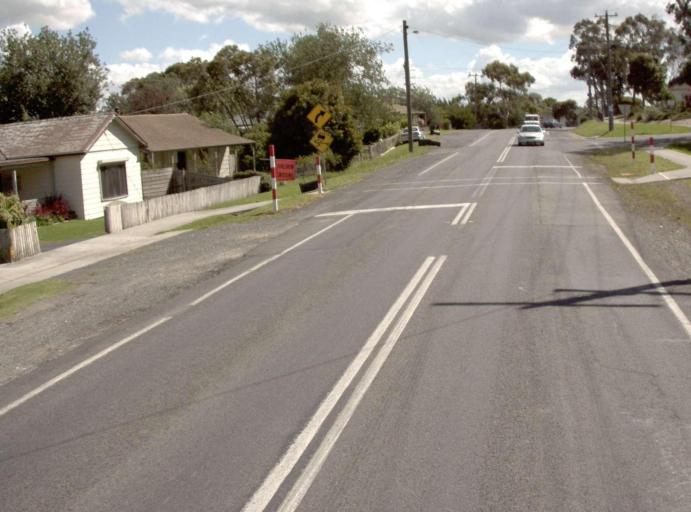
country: AU
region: Victoria
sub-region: Latrobe
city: Traralgon
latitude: -38.1490
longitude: 146.4795
